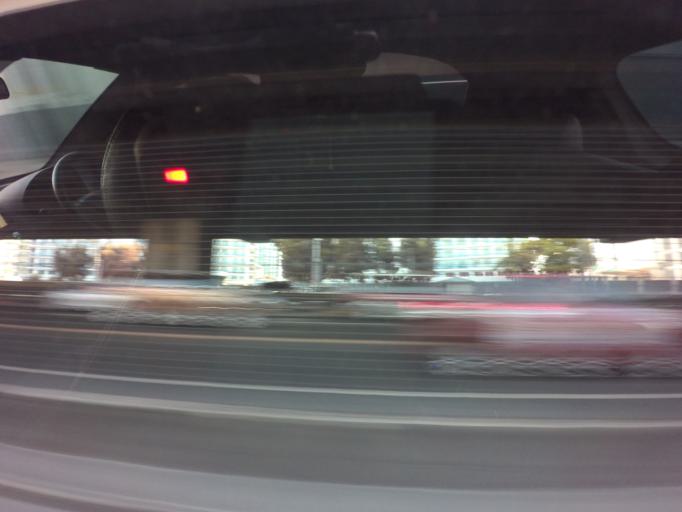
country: PH
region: Calabarzon
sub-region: Province of Rizal
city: Taguig
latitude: 14.4845
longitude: 121.0453
